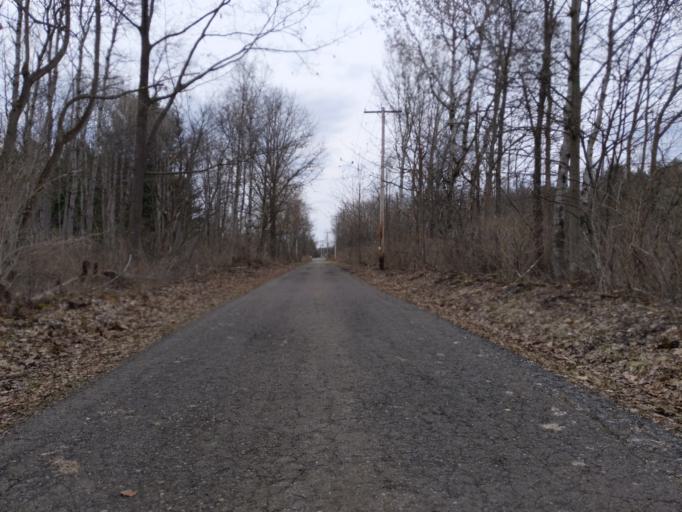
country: US
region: New York
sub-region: Tompkins County
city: Dryden
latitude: 42.5094
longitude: -76.3433
